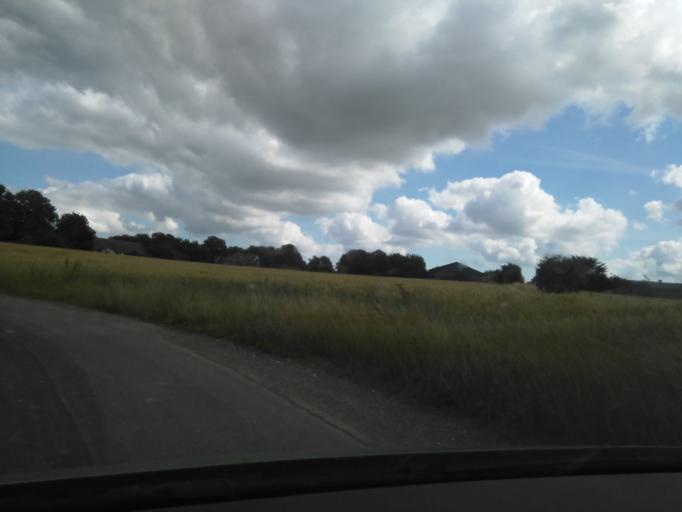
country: DK
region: Central Jutland
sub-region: Arhus Kommune
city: Solbjerg
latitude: 56.0058
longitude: 10.0504
